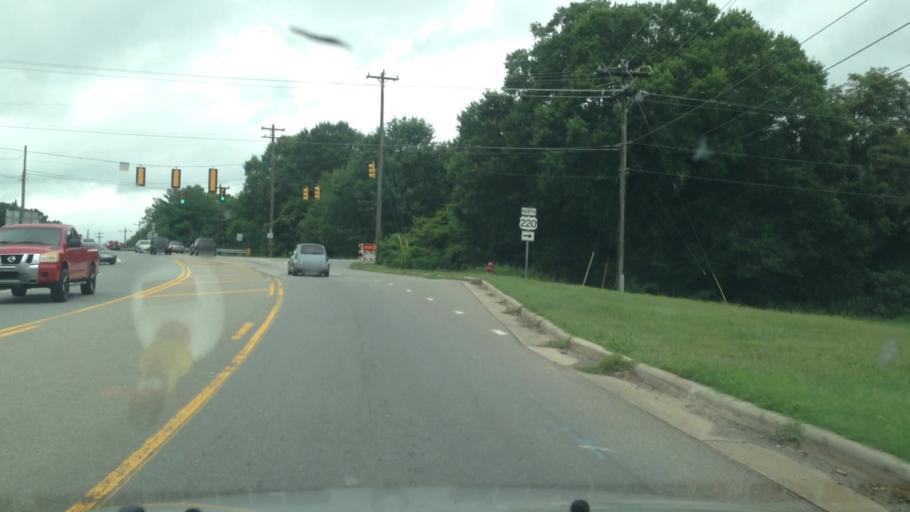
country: US
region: North Carolina
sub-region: Rockingham County
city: Mayodan
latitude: 36.4173
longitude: -79.9362
